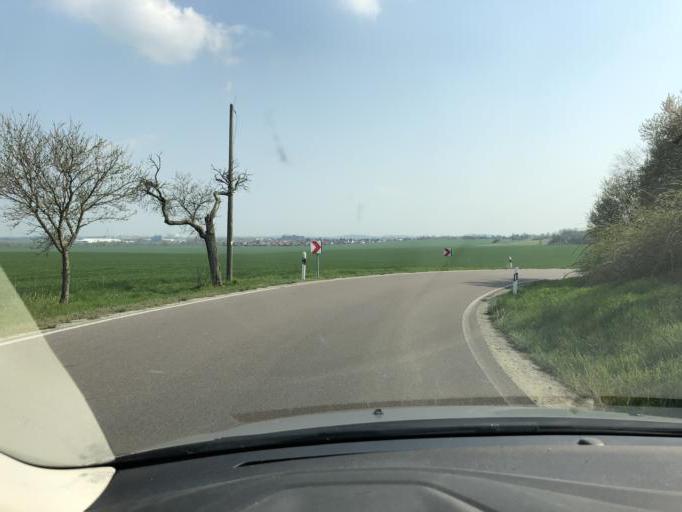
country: DE
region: Saxony-Anhalt
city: Niemberg
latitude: 51.5624
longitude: 12.0731
